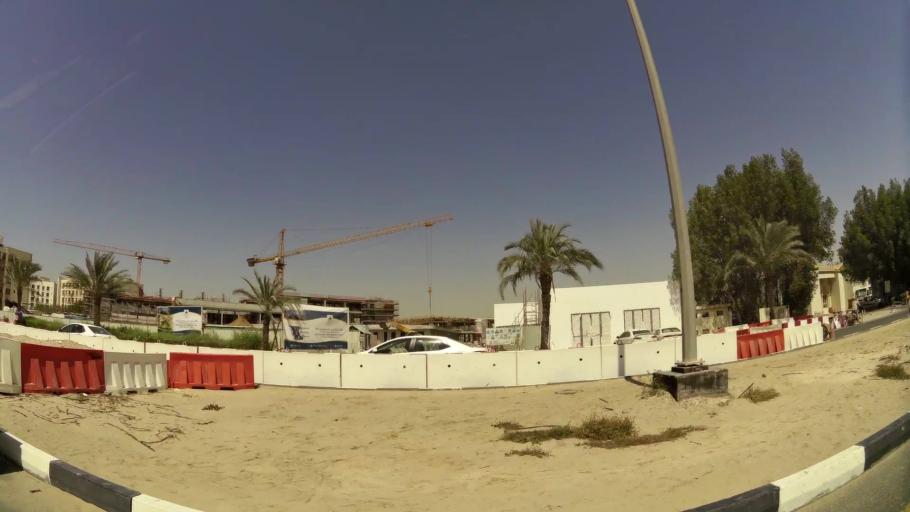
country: AE
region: Dubai
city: Dubai
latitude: 24.9975
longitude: 55.1543
